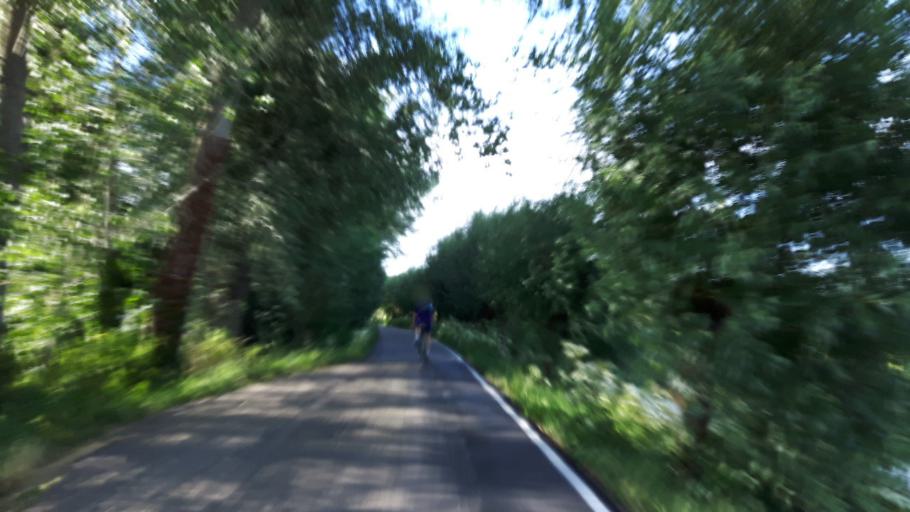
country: NL
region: Utrecht
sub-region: Gemeente Oudewater
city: Oudewater
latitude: 52.0290
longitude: 4.8837
